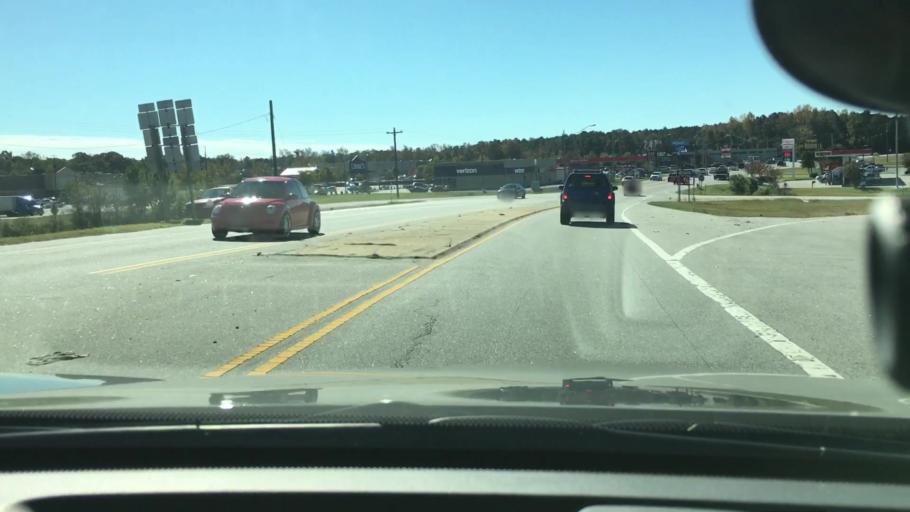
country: US
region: North Carolina
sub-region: Edgecombe County
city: Princeville
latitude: 35.8860
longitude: -77.5475
